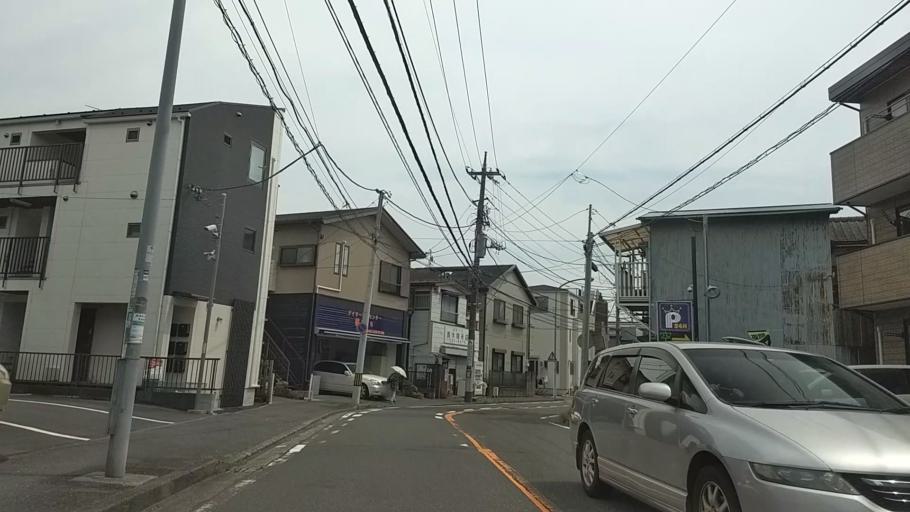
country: JP
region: Kanagawa
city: Yokohama
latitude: 35.4334
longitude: 139.6071
